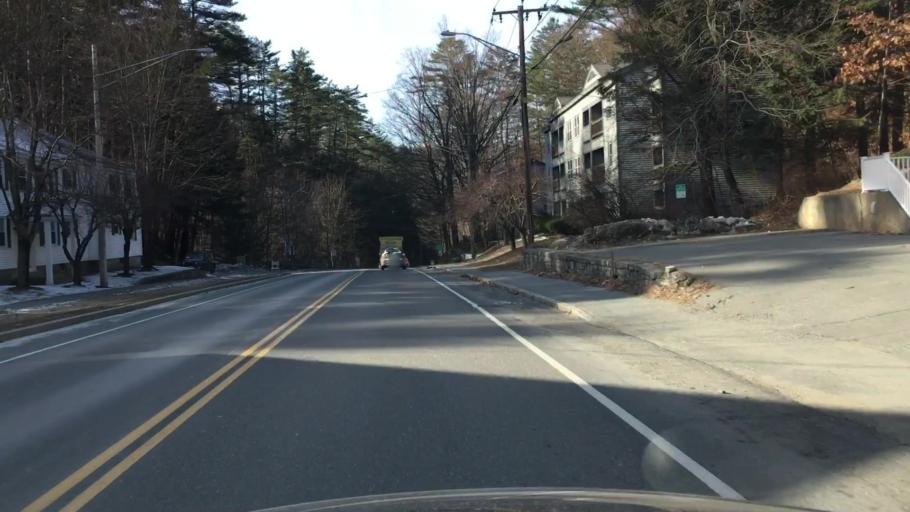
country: US
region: New Hampshire
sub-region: Grafton County
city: Hanover
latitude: 43.7028
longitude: -72.2953
